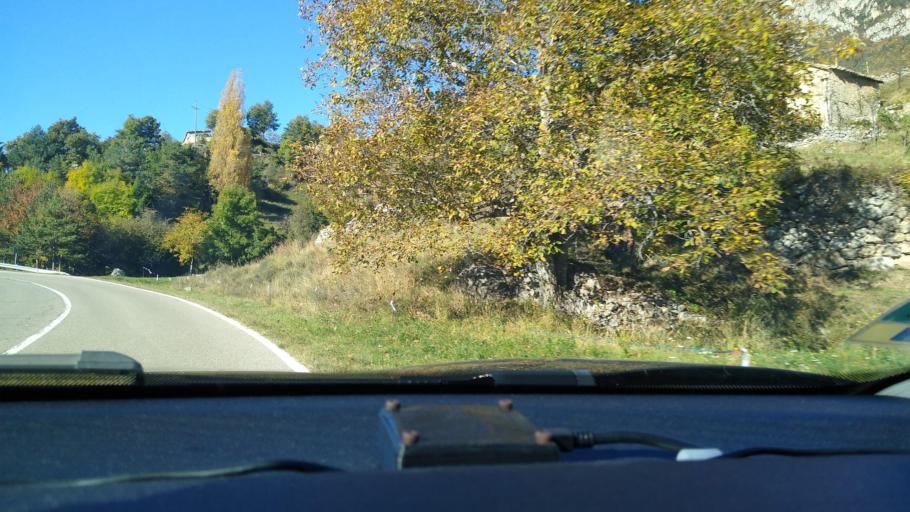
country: ES
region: Catalonia
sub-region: Provincia de Barcelona
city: Saldes
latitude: 42.2249
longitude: 1.7313
